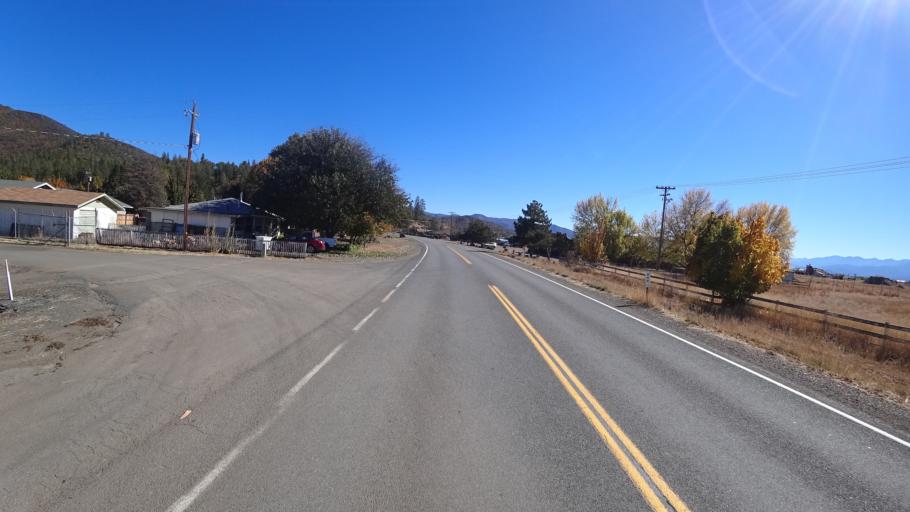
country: US
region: California
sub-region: Siskiyou County
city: Yreka
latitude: 41.6029
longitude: -122.8493
